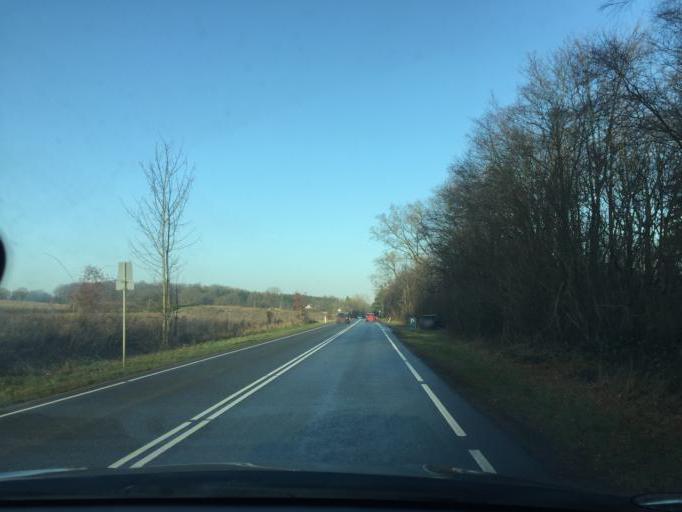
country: DK
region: South Denmark
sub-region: Faaborg-Midtfyn Kommune
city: Faaborg
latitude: 55.1515
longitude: 10.2676
